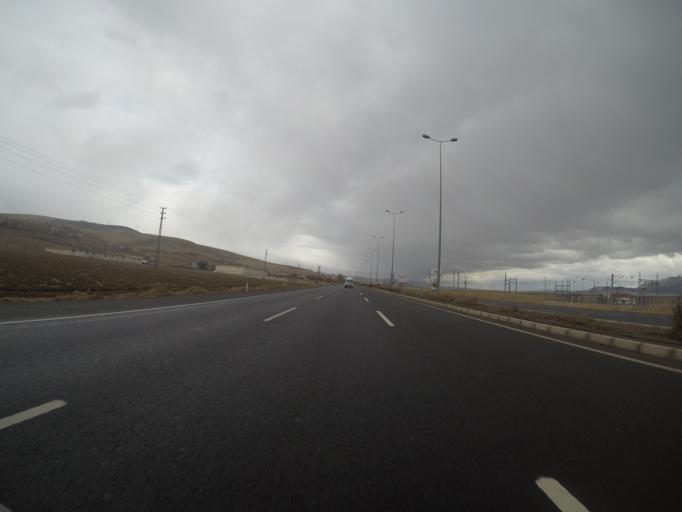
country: TR
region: Kayseri
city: Incesu
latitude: 38.7197
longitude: 35.2717
